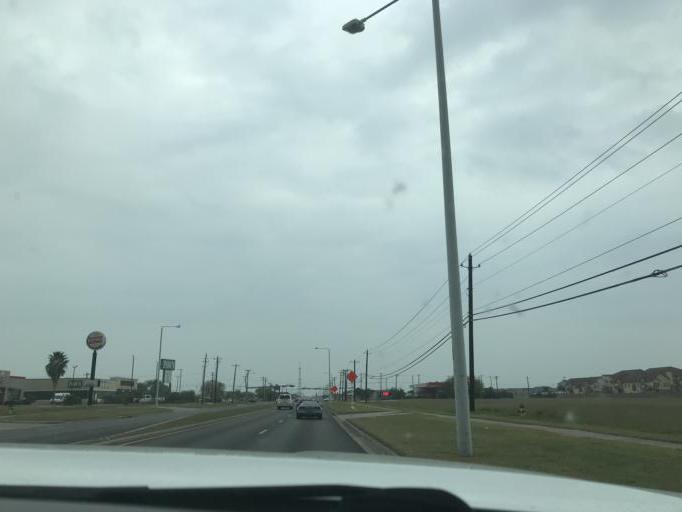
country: US
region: Texas
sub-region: Nueces County
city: Corpus Christi
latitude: 27.6769
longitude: -97.3666
